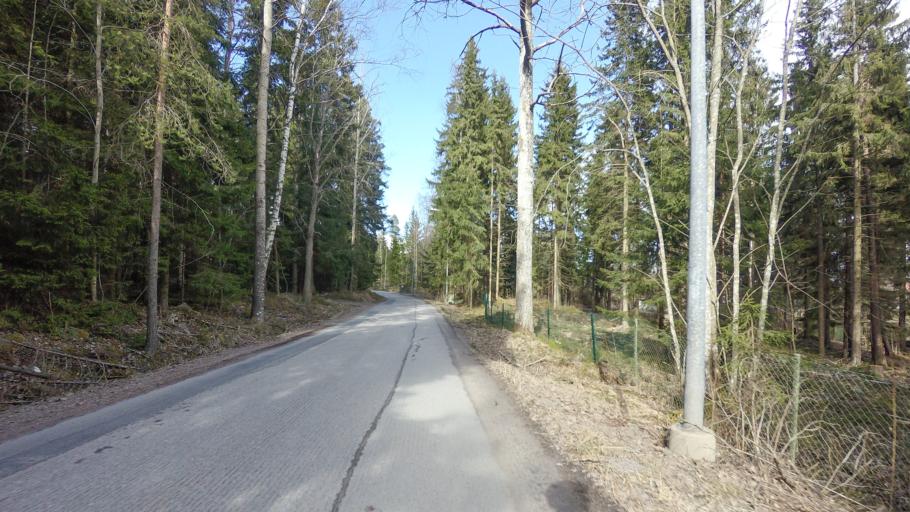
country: FI
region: Uusimaa
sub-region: Helsinki
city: Vantaa
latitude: 60.1935
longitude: 25.1038
